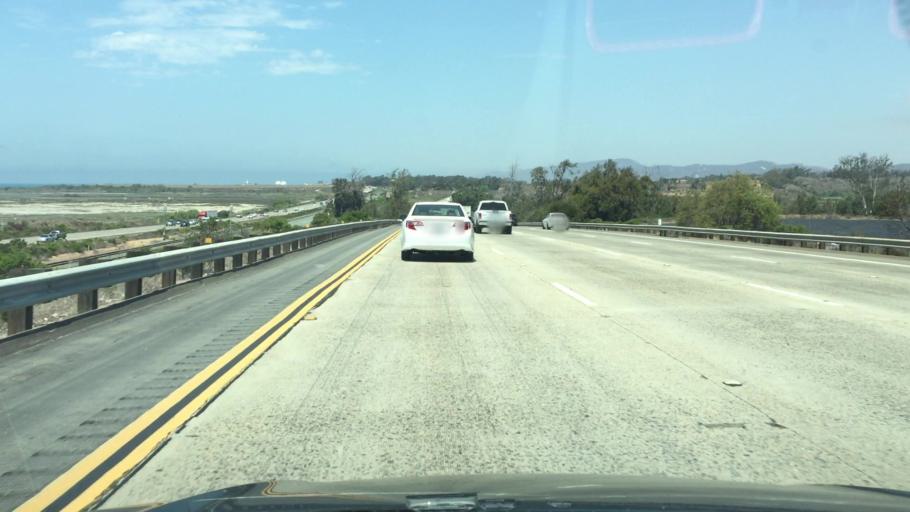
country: US
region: California
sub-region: San Diego County
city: Camp Pendleton South
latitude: 33.2281
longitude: -117.3974
